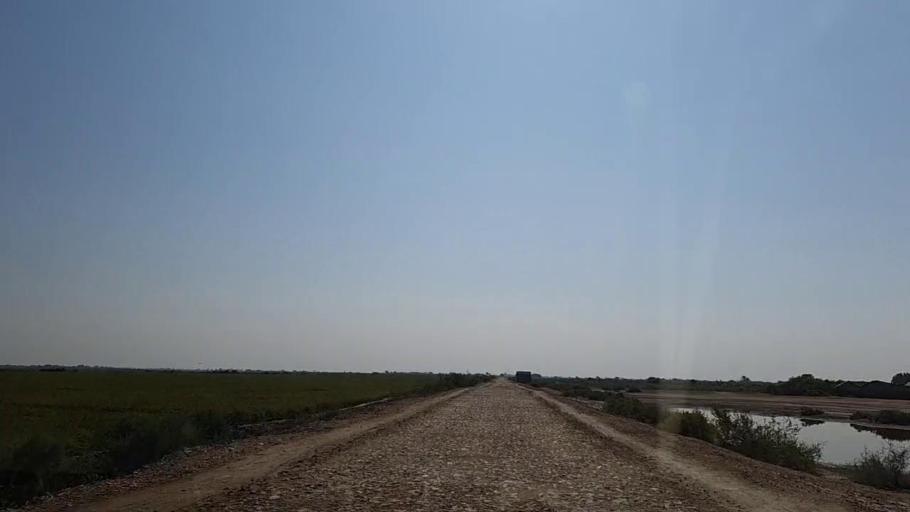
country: PK
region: Sindh
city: Chuhar Jamali
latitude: 24.4732
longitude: 68.0913
